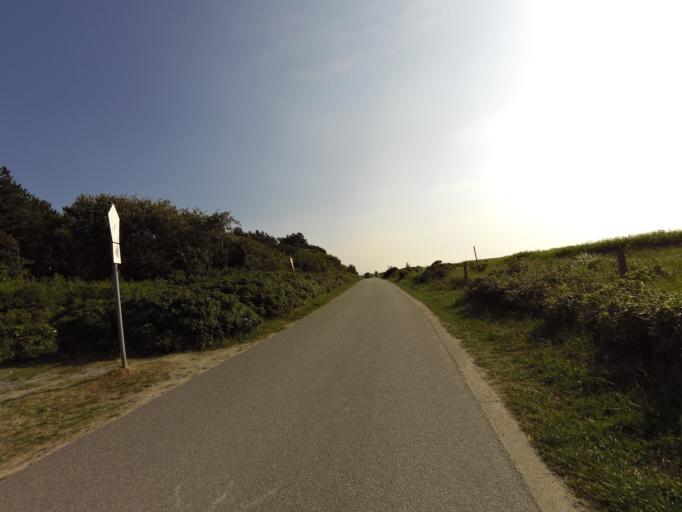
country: DE
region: Lower Saxony
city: Nordholz
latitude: 53.8684
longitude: 8.6022
